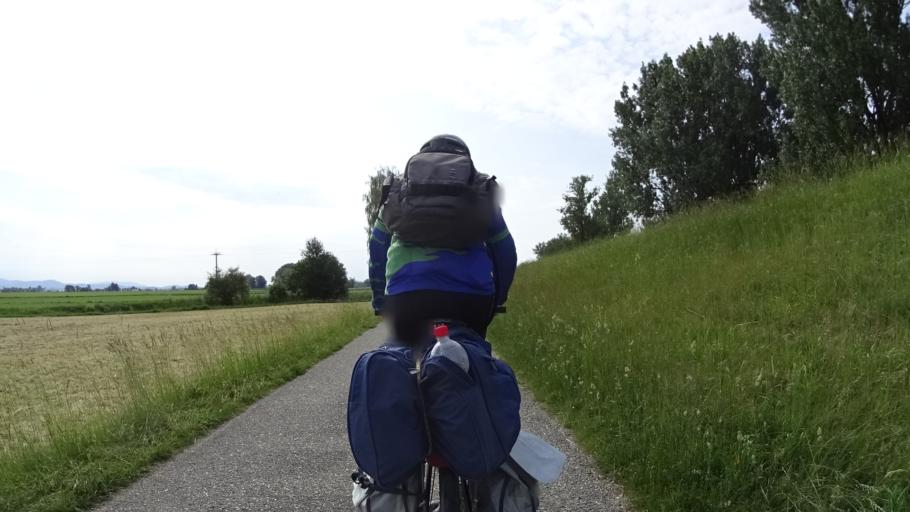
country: DE
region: Bavaria
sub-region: Lower Bavaria
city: Irlbach
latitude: 48.8381
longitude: 12.7754
